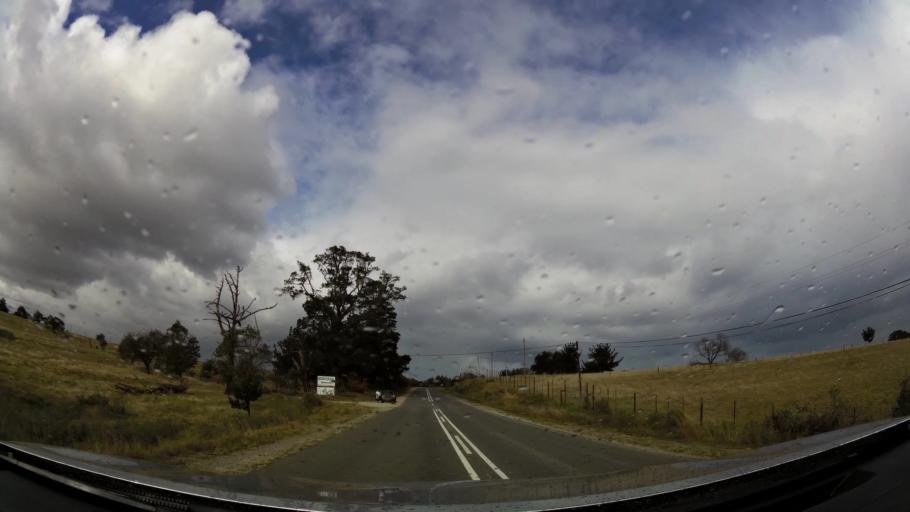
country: ZA
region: Western Cape
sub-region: Eden District Municipality
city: George
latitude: -34.0364
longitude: 22.3232
